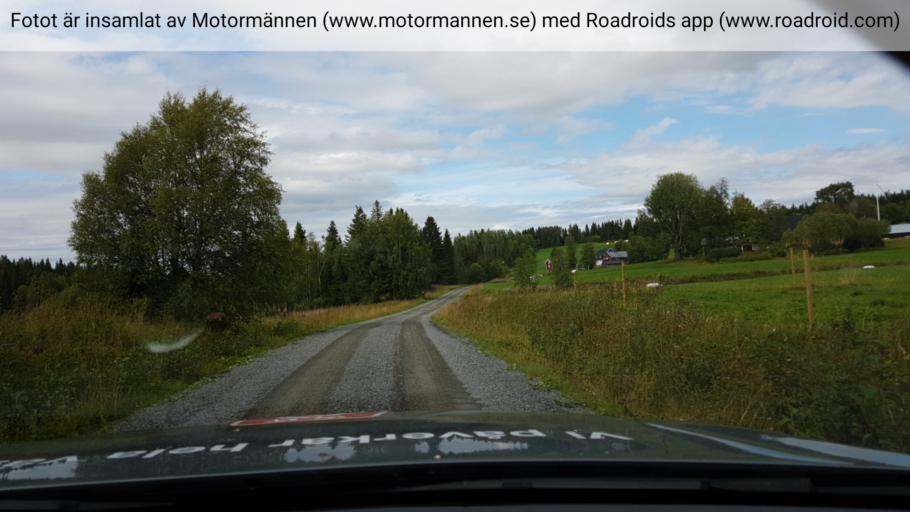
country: SE
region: Jaemtland
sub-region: Krokoms Kommun
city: Valla
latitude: 63.5235
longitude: 13.8876
